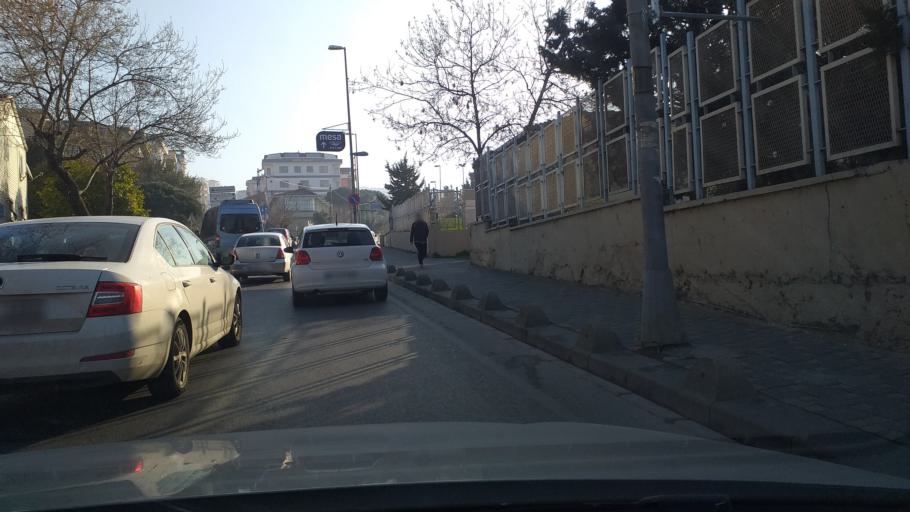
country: TR
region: Istanbul
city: Maltepe
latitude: 40.9317
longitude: 29.1475
